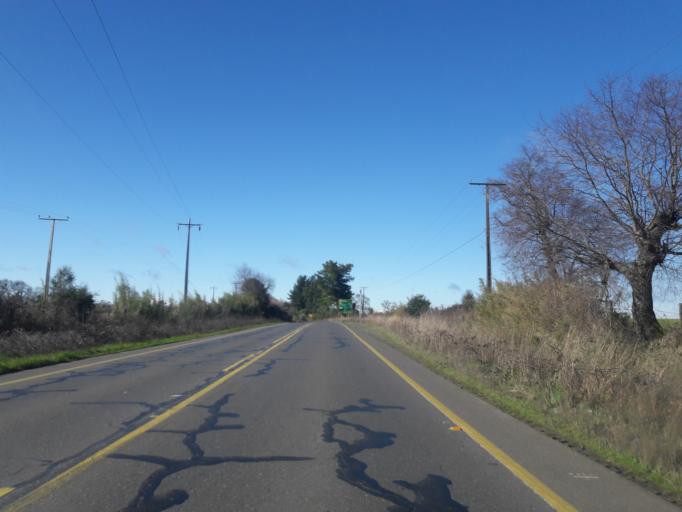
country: CL
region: Araucania
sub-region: Provincia de Malleco
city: Victoria
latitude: -38.2510
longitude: -72.2992
